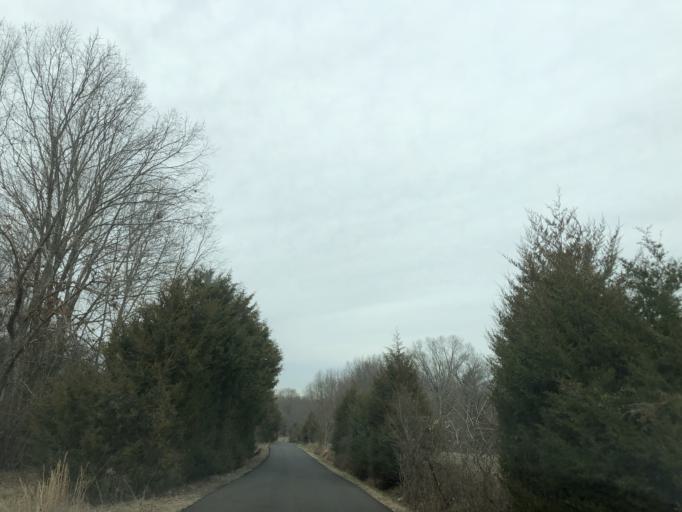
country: US
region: Tennessee
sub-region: Robertson County
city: Greenbrier
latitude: 36.4624
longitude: -86.7897
